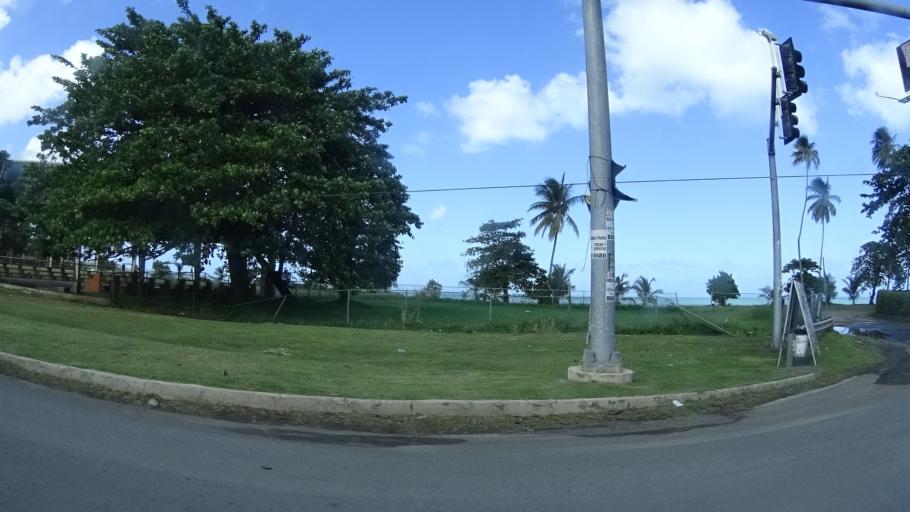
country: PR
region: Luquillo
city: Playa Fortuna
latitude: 18.3794
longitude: -65.7396
